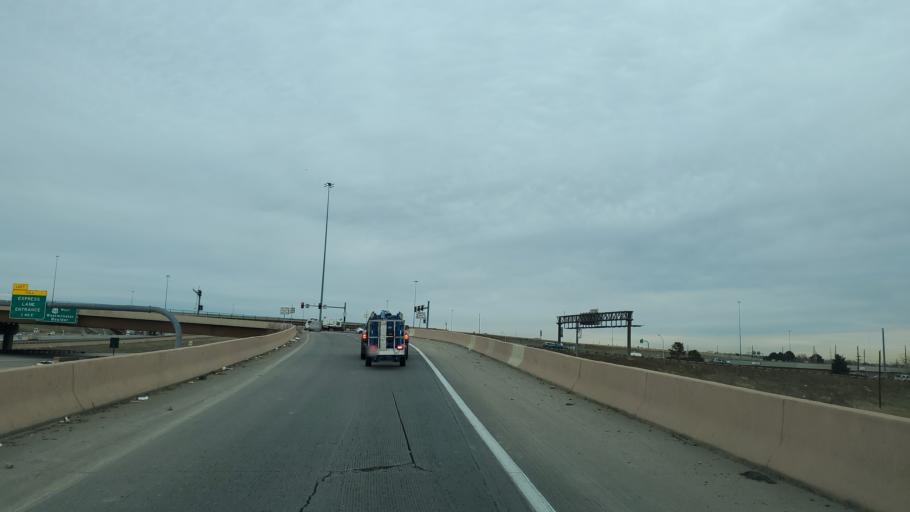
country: US
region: Colorado
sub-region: Adams County
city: Twin Lakes
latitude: 39.8224
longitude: -104.9819
